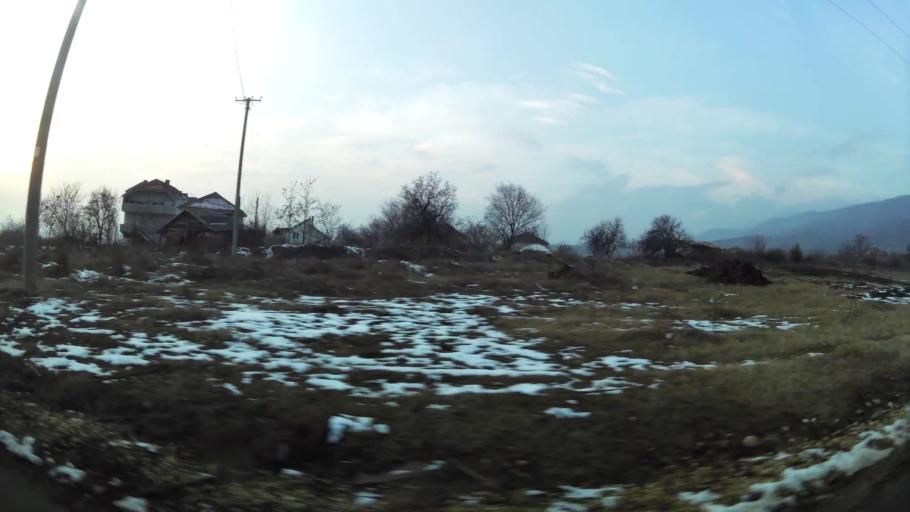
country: MK
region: Aracinovo
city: Arachinovo
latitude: 42.0303
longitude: 21.5474
